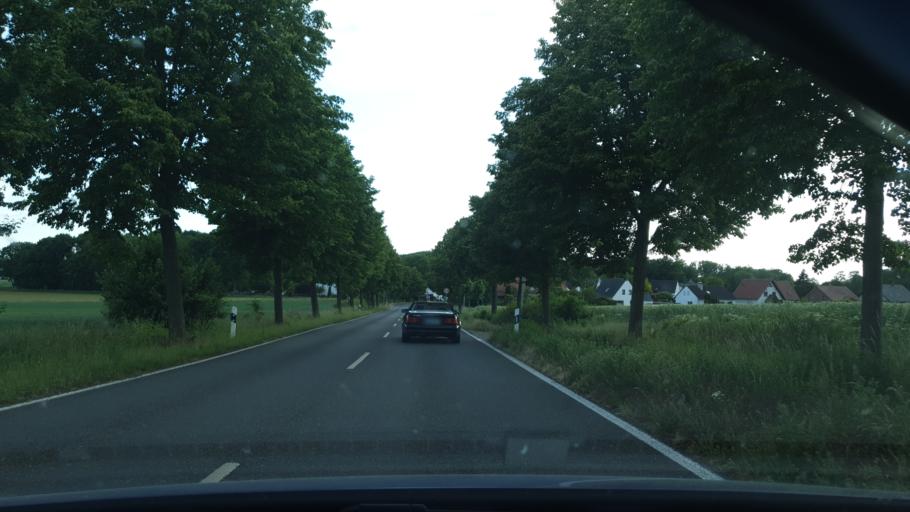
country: DE
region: North Rhine-Westphalia
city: Enger
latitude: 52.1780
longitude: 8.5454
